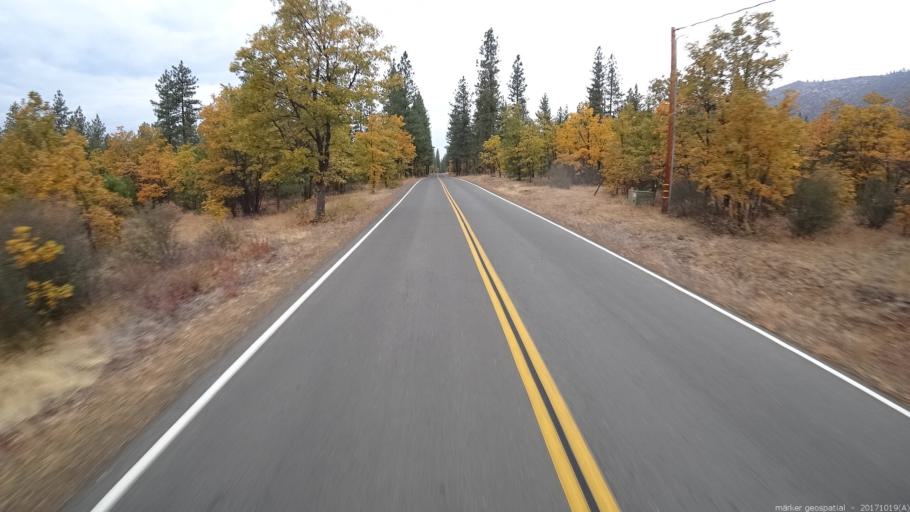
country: US
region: California
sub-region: Shasta County
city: Burney
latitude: 41.1674
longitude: -121.3590
